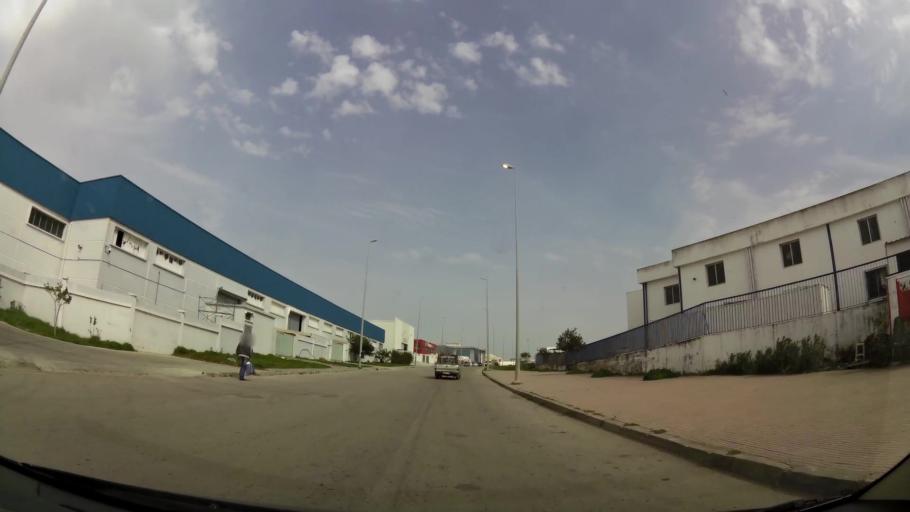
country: MA
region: Tanger-Tetouan
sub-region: Tanger-Assilah
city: Boukhalef
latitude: 35.7156
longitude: -5.9001
